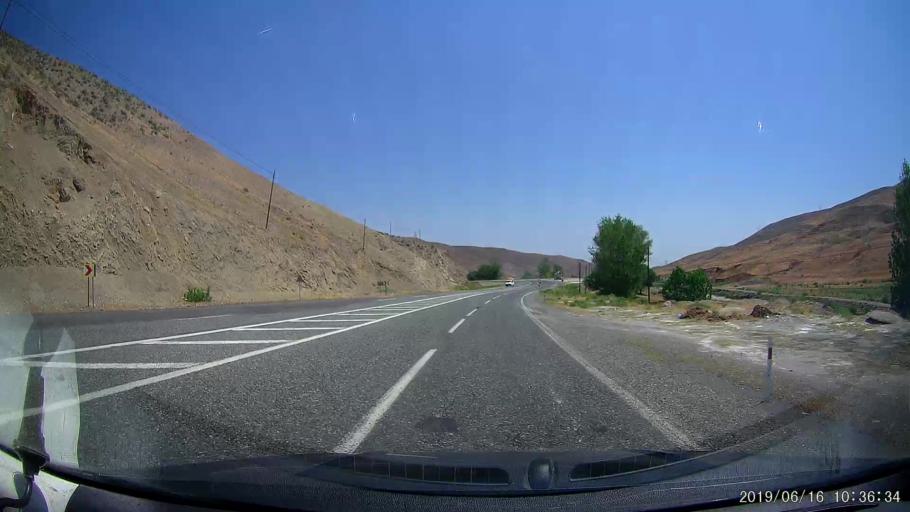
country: TR
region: Igdir
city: Tuzluca
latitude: 40.0397
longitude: 43.6832
